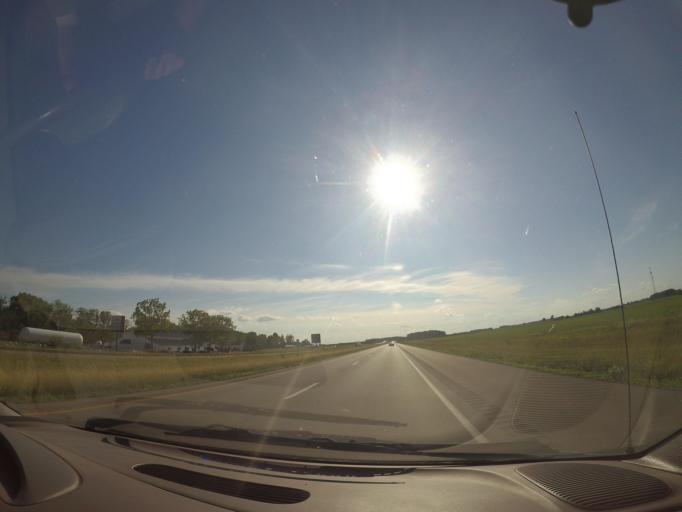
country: US
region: Ohio
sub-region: Henry County
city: Liberty Center
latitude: 41.4156
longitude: -84.0481
